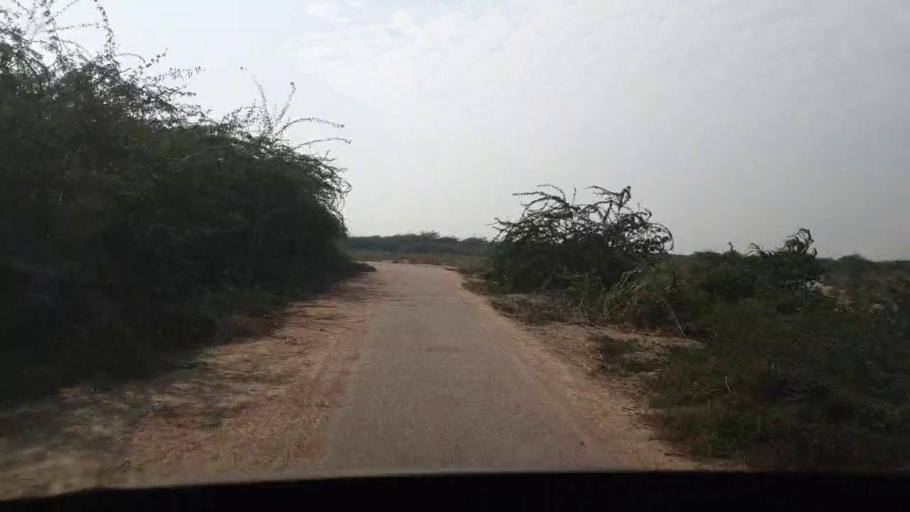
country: PK
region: Sindh
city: Chuhar Jamali
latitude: 24.2402
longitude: 67.9858
